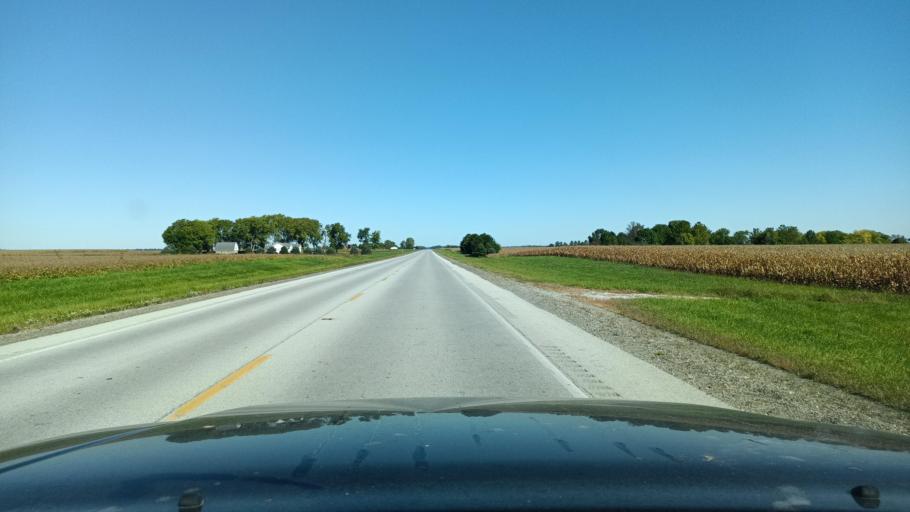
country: US
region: Illinois
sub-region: Champaign County
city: Philo
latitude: 40.0307
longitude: -88.1616
